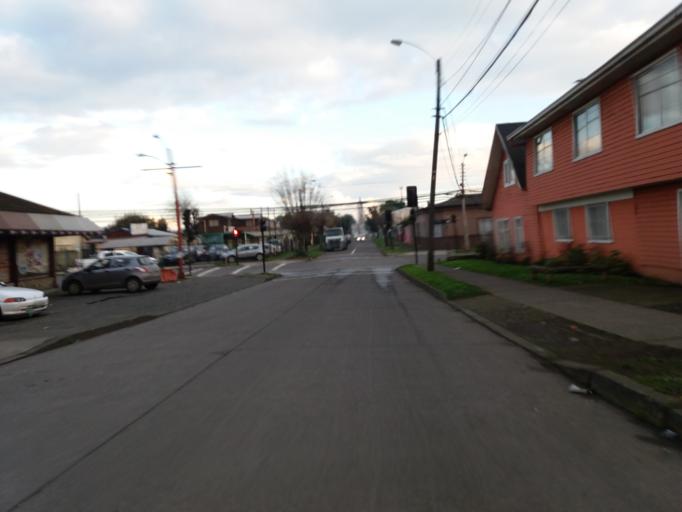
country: CL
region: Araucania
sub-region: Provincia de Cautin
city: Temuco
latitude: -38.7395
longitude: -72.6083
